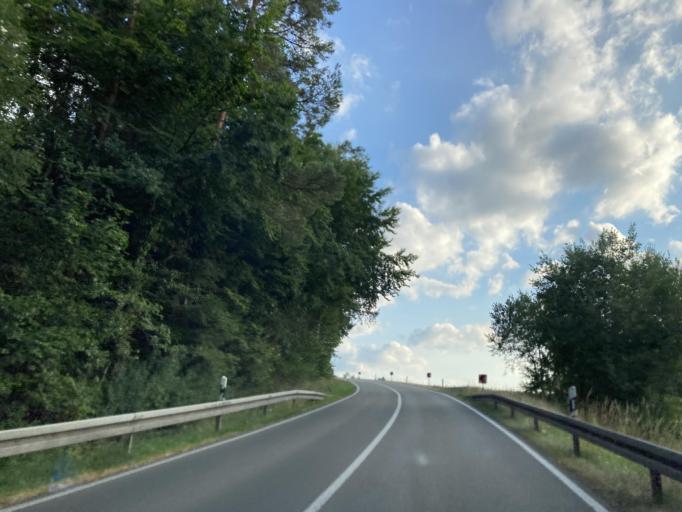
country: DE
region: Baden-Wuerttemberg
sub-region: Karlsruhe Region
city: Neubulach
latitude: 48.6287
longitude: 8.6532
